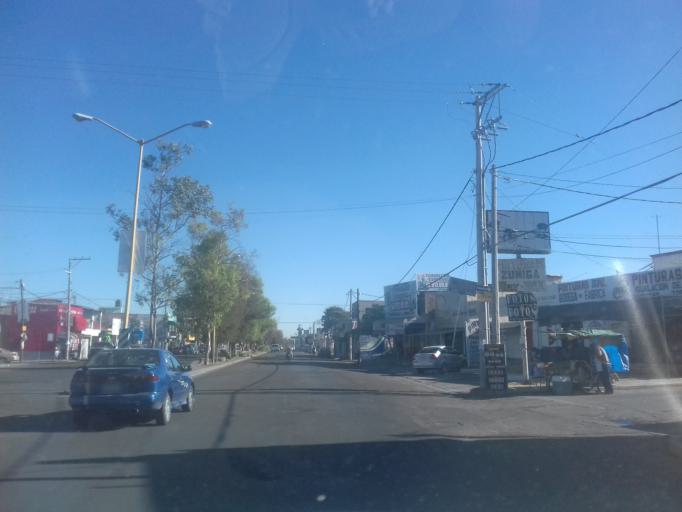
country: MX
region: Aguascalientes
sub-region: Aguascalientes
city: Aguascalientes
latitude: 21.8539
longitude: -102.2692
